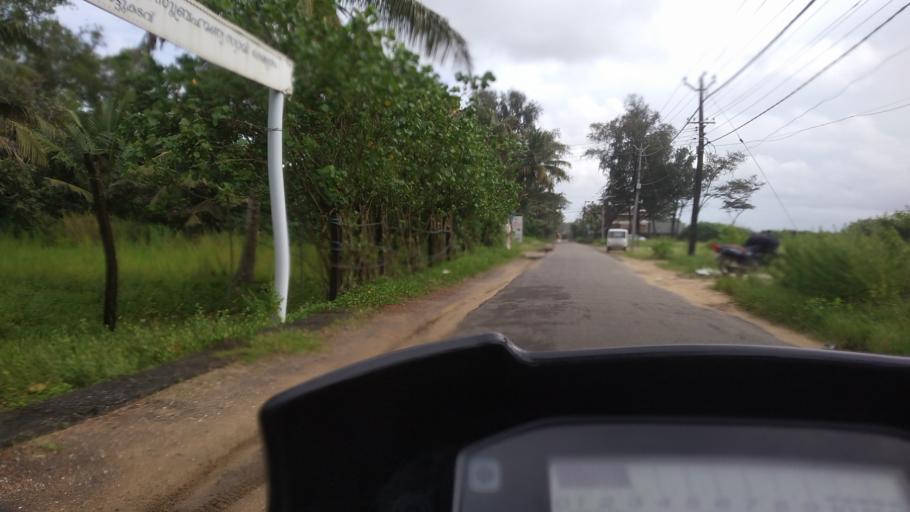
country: IN
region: Kerala
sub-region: Thrissur District
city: Kodungallur
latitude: 10.1496
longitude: 76.1759
